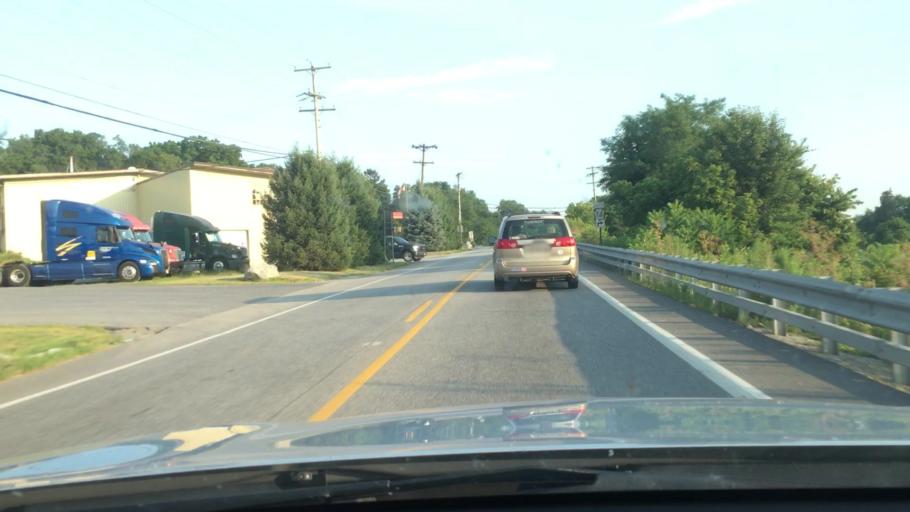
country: US
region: Pennsylvania
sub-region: York County
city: Dillsburg
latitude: 40.1214
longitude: -77.0359
